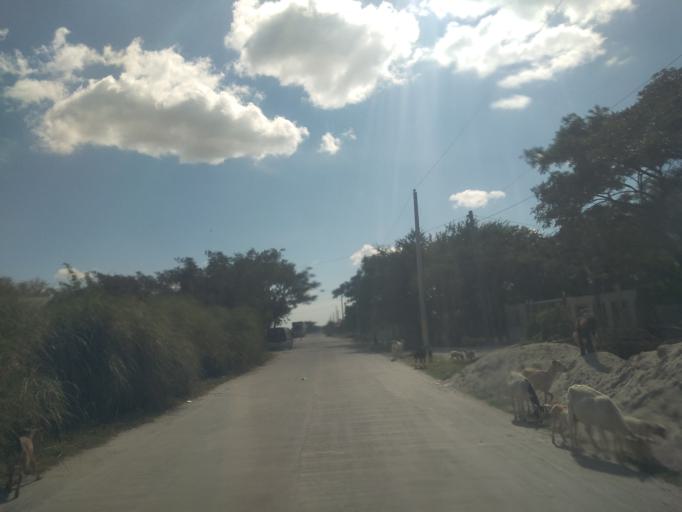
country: PH
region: Central Luzon
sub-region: Province of Pampanga
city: Balas
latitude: 15.0584
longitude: 120.5976
